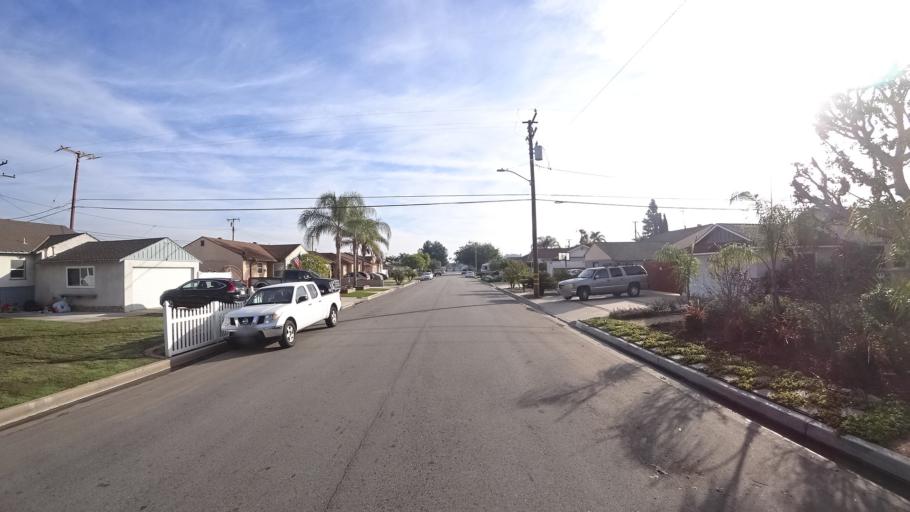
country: US
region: California
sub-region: Orange County
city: Garden Grove
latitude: 33.7929
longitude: -117.9298
